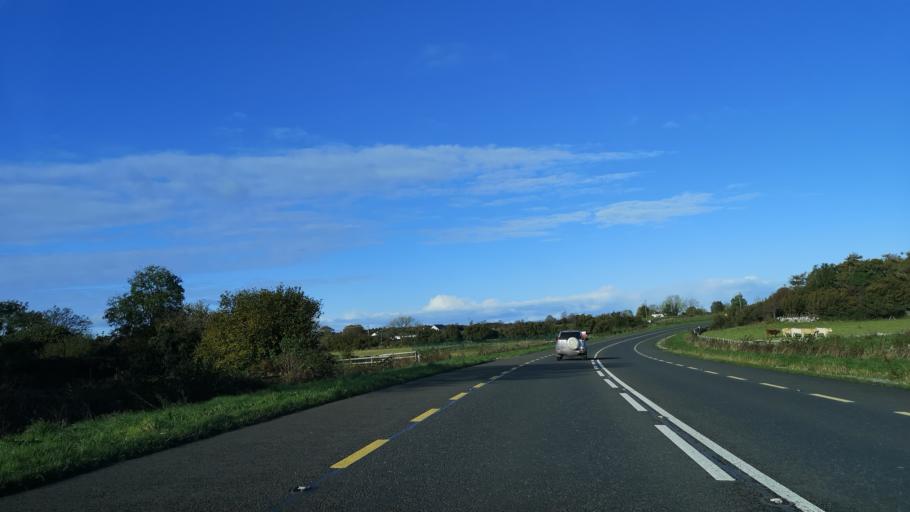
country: IE
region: Connaught
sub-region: County Galway
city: Claregalway
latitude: 53.4279
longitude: -9.0513
